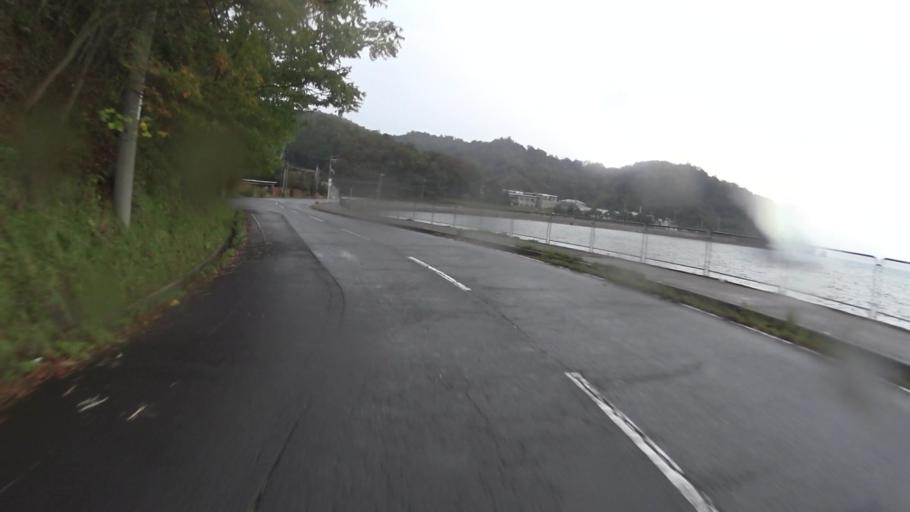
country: JP
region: Kyoto
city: Miyazu
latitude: 35.5641
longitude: 135.2137
